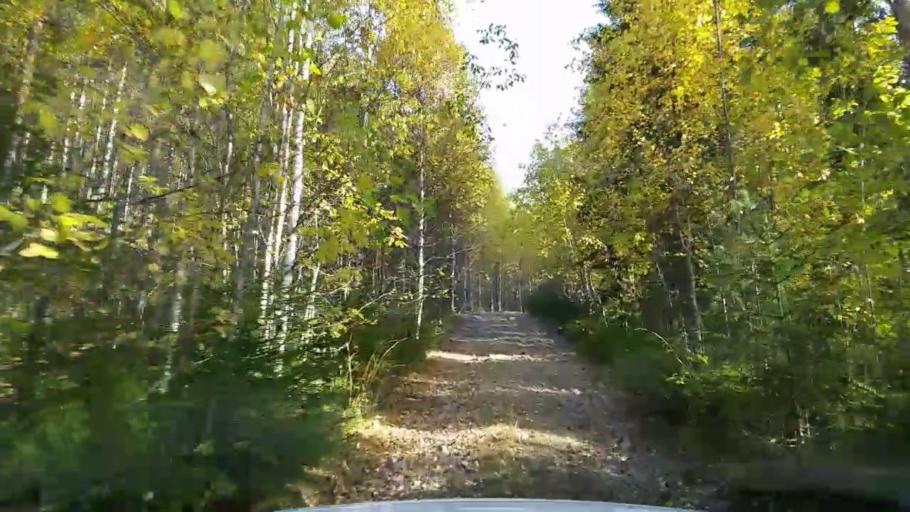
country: SE
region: Gaevleborg
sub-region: Ljusdals Kommun
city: Jaervsoe
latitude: 61.7802
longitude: 16.1926
